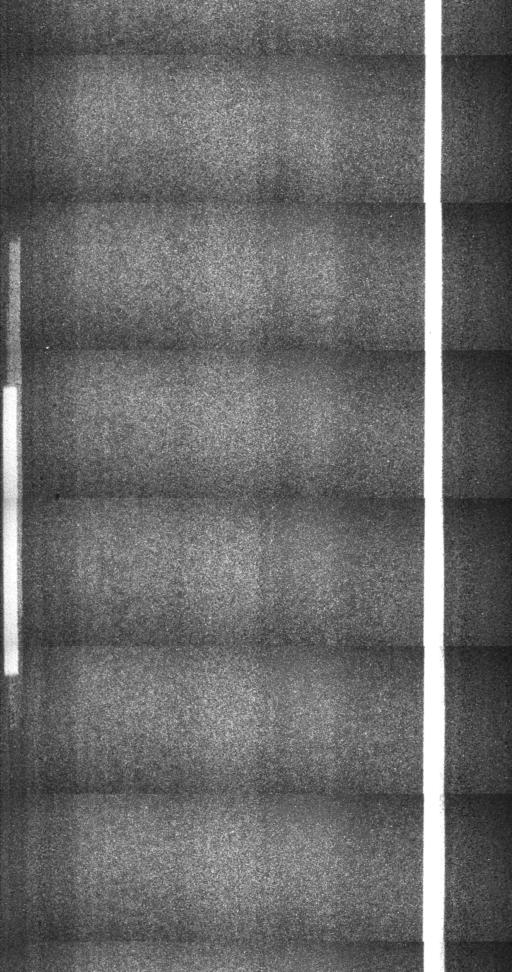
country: US
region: Vermont
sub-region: Windham County
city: Dover
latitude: 42.9789
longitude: -72.8884
